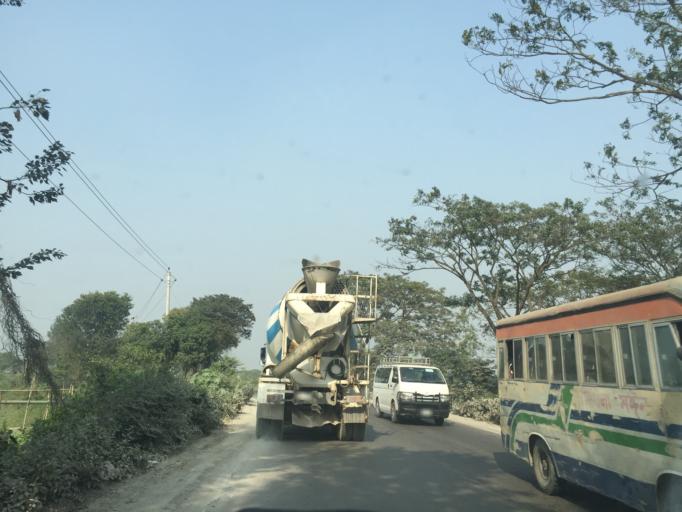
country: BD
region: Dhaka
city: Tungi
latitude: 23.8412
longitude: 90.3430
